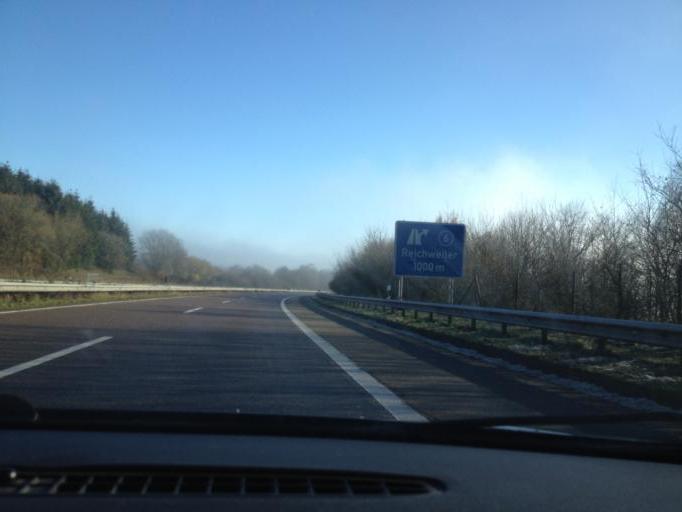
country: DE
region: Rheinland-Pfalz
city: Reichweiler
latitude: 49.5415
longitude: 7.2761
